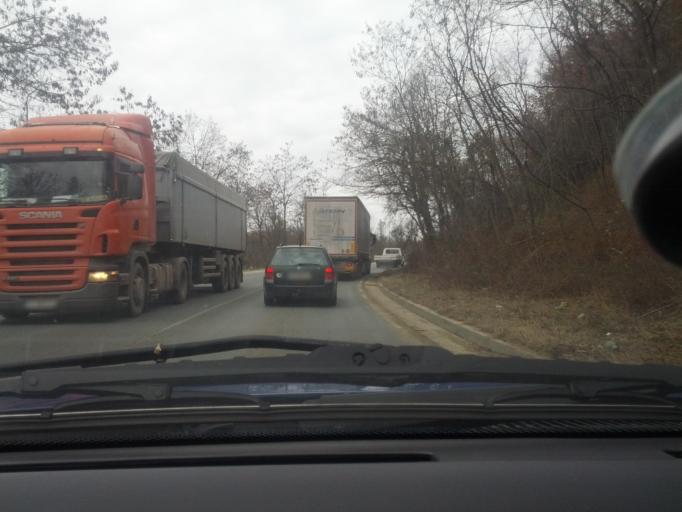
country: BG
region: Vratsa
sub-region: Obshtina Mezdra
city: Mezdra
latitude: 43.0184
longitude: 23.6874
